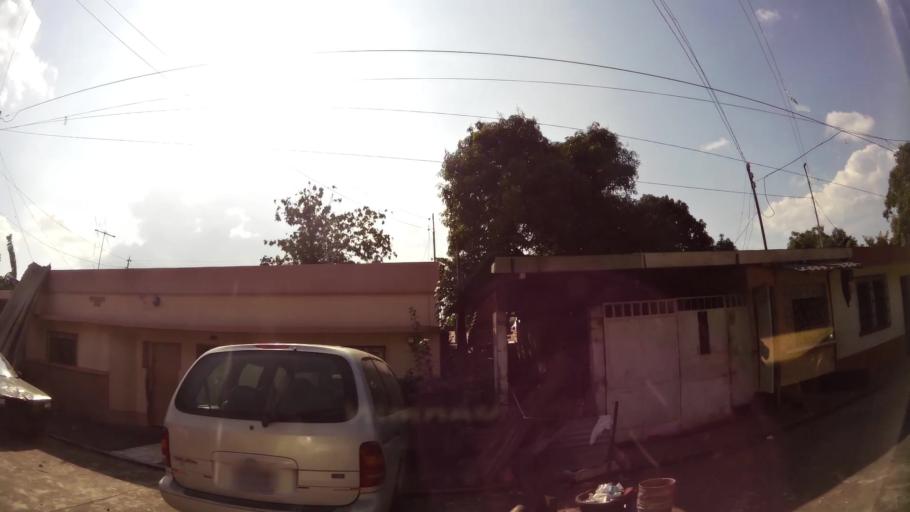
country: GT
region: Retalhuleu
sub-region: Municipio de Retalhuleu
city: Retalhuleu
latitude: 14.5436
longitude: -91.6801
